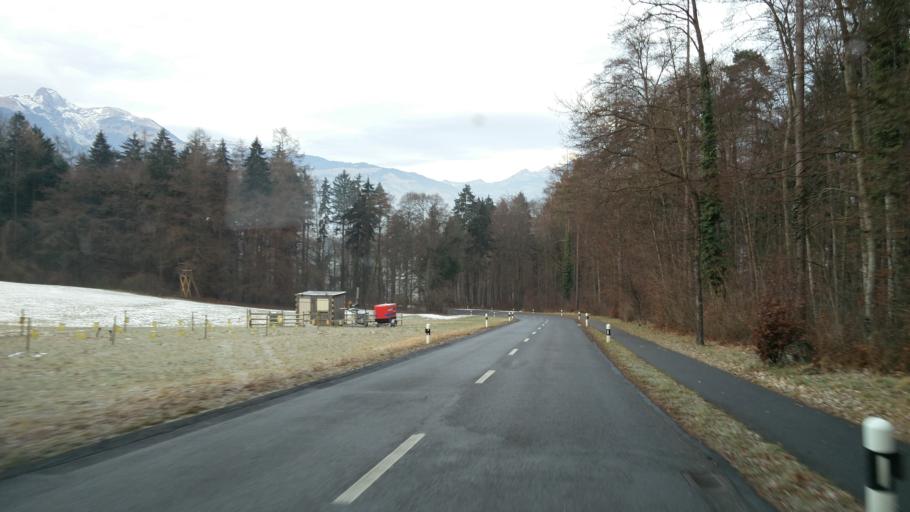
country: LI
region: Planken
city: Planken
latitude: 47.1733
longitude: 9.5312
